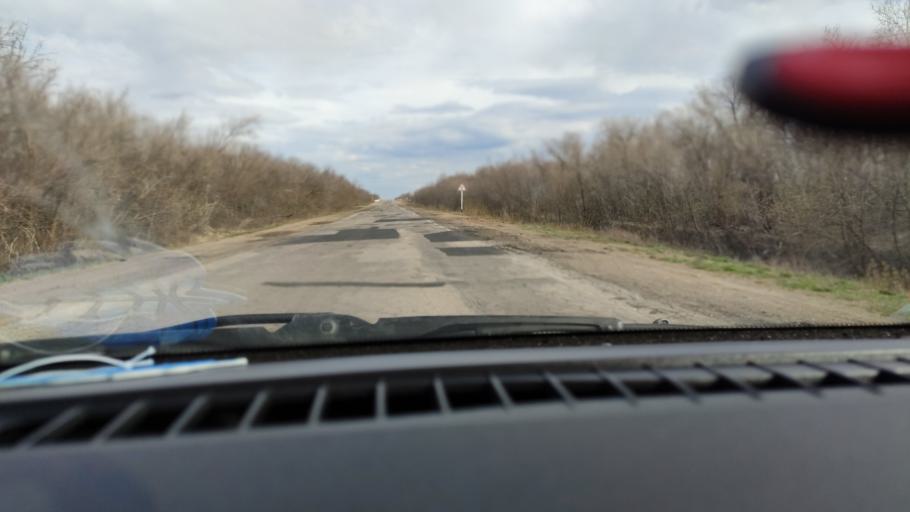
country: RU
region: Saratov
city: Krasnoarmeysk
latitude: 51.0737
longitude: 45.9813
